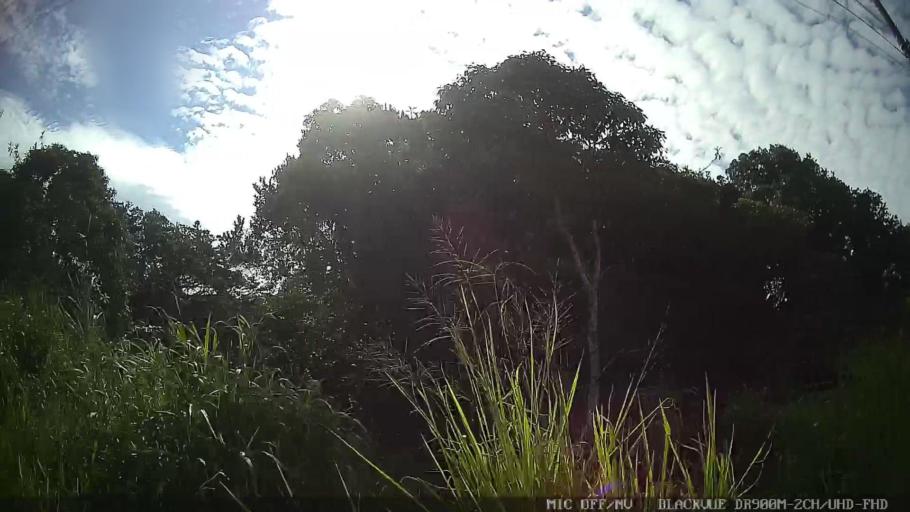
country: BR
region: Sao Paulo
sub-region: Itanhaem
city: Itanhaem
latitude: -24.1559
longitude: -46.7434
